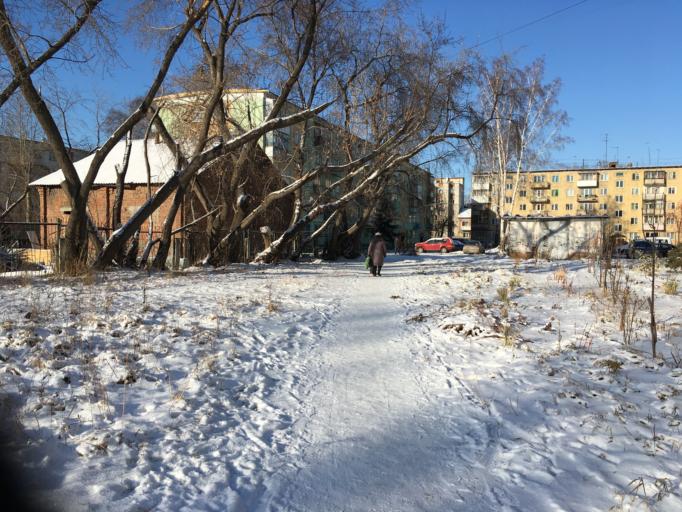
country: RU
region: Novosibirsk
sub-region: Novosibirskiy Rayon
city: Novosibirsk
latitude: 55.0546
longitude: 82.9694
